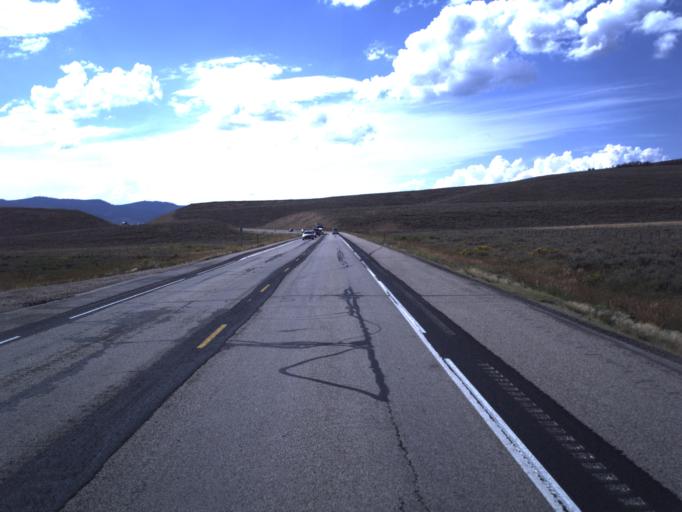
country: US
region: Utah
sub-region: Wasatch County
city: Heber
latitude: 40.2286
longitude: -111.1173
